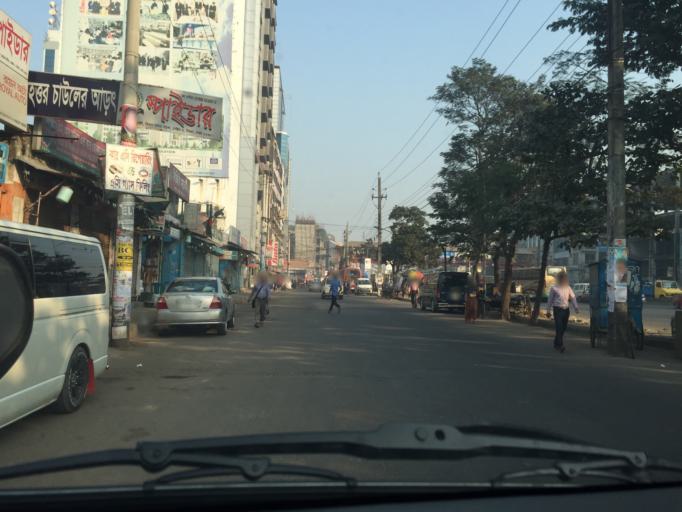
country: BD
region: Dhaka
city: Tungi
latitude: 23.8729
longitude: 90.4003
